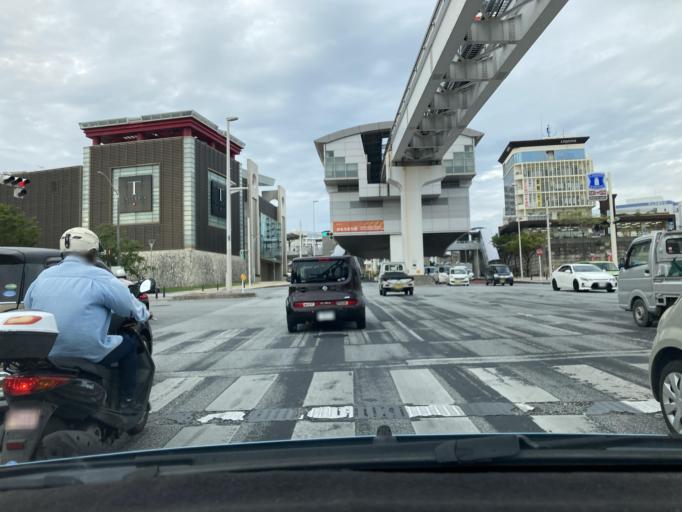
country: JP
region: Okinawa
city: Naha-shi
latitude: 26.2217
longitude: 127.6984
